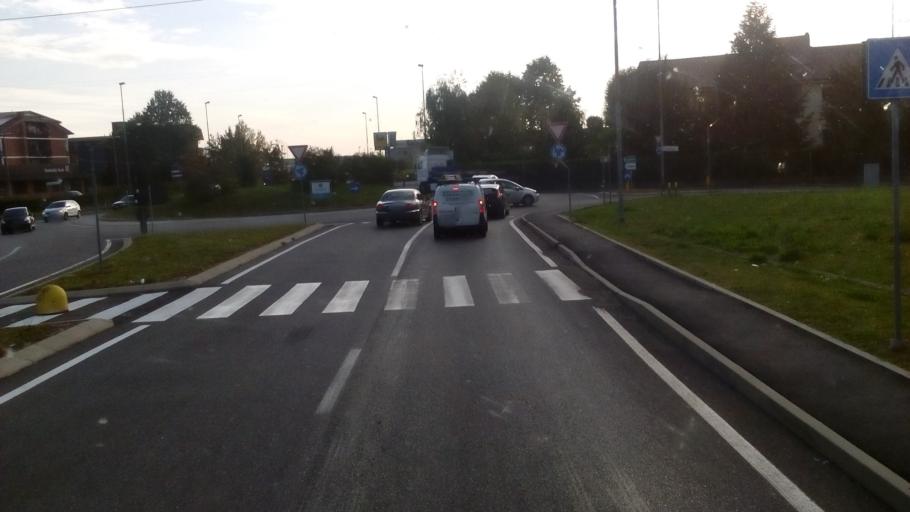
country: IT
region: Lombardy
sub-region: Provincia di Como
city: Novedrate
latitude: 45.6971
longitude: 9.1280
